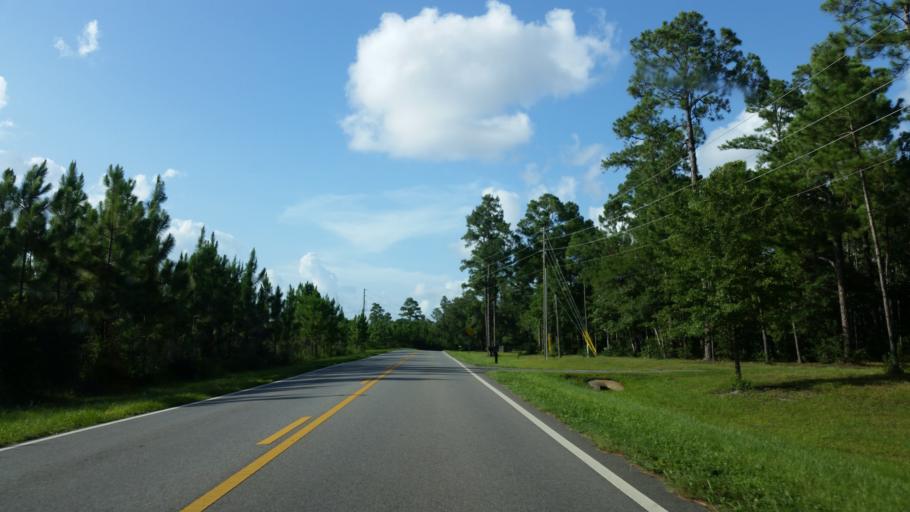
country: US
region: Florida
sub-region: Santa Rosa County
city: Bagdad
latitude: 30.5309
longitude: -87.0536
